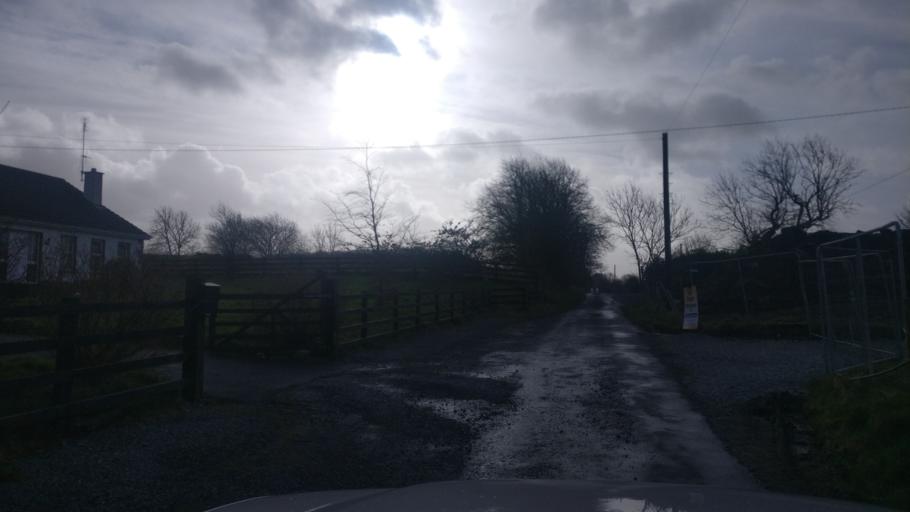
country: IE
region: Connaught
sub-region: County Galway
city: Loughrea
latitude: 53.2759
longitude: -8.5944
